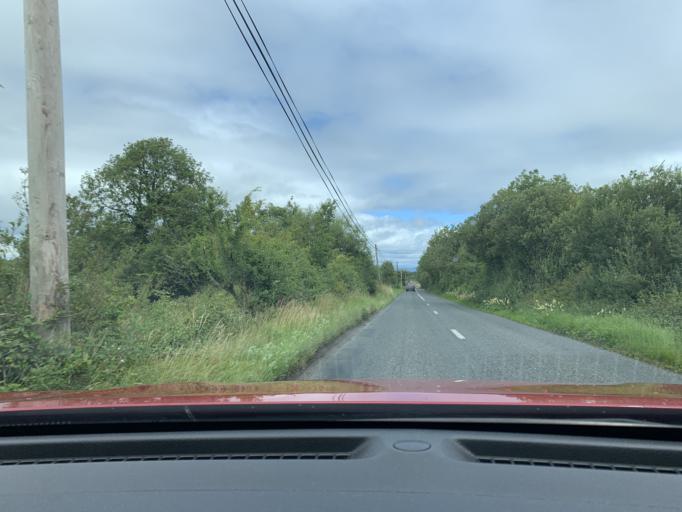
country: IE
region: Connaught
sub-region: County Leitrim
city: Carrick-on-Shannon
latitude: 53.9051
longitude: -8.1324
